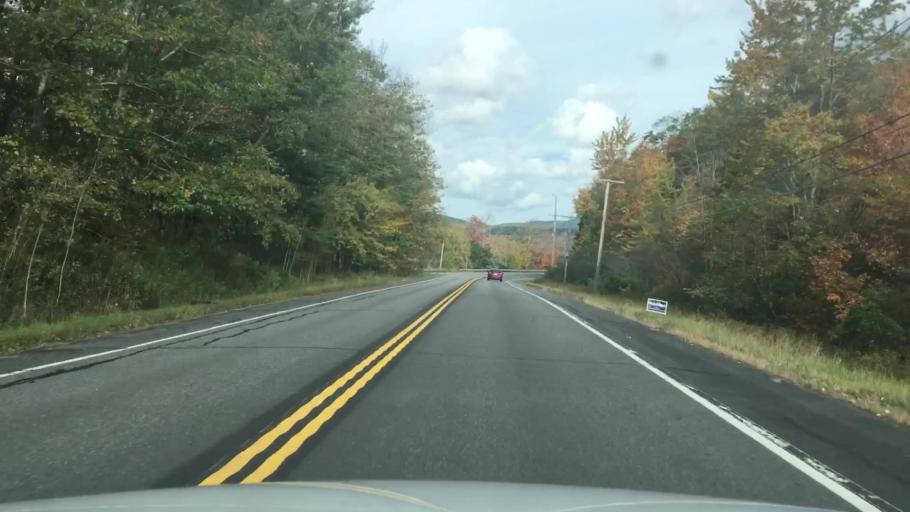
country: US
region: Maine
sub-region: Knox County
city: Rockport
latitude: 44.1653
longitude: -69.1192
